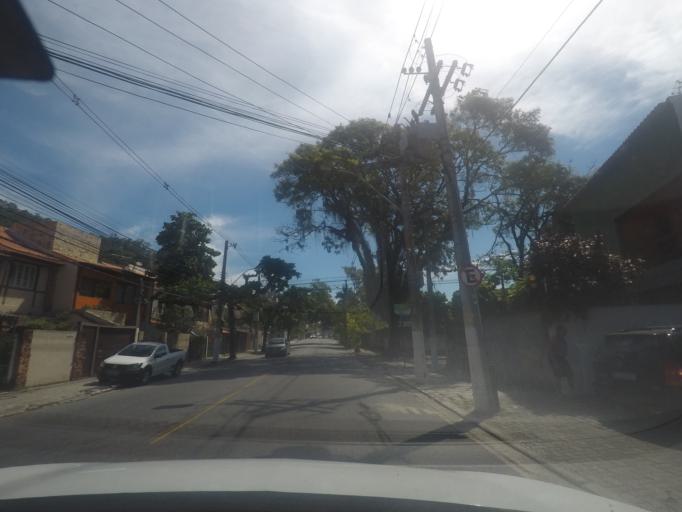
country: BR
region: Rio de Janeiro
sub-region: Niteroi
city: Niteroi
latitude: -22.9181
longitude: -43.0863
